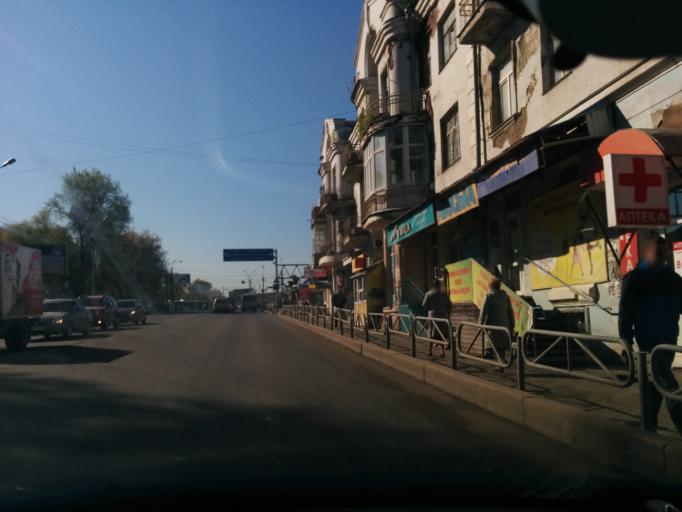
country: RU
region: Perm
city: Perm
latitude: 58.0050
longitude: 56.2295
